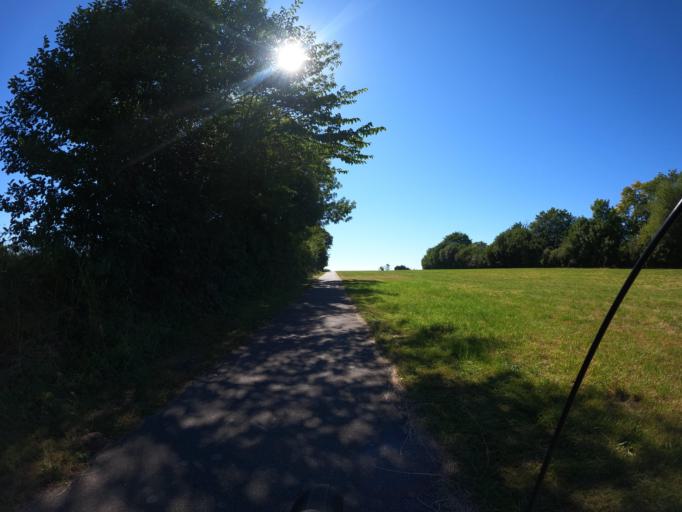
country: DE
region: Schleswig-Holstein
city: Steinberg
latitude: 54.7840
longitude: 9.7979
